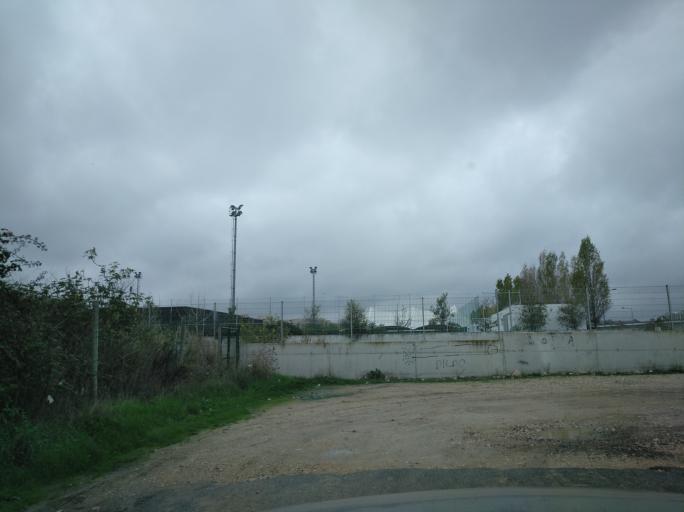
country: PT
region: Lisbon
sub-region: Loures
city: Sacavem
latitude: 38.7945
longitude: -9.0944
